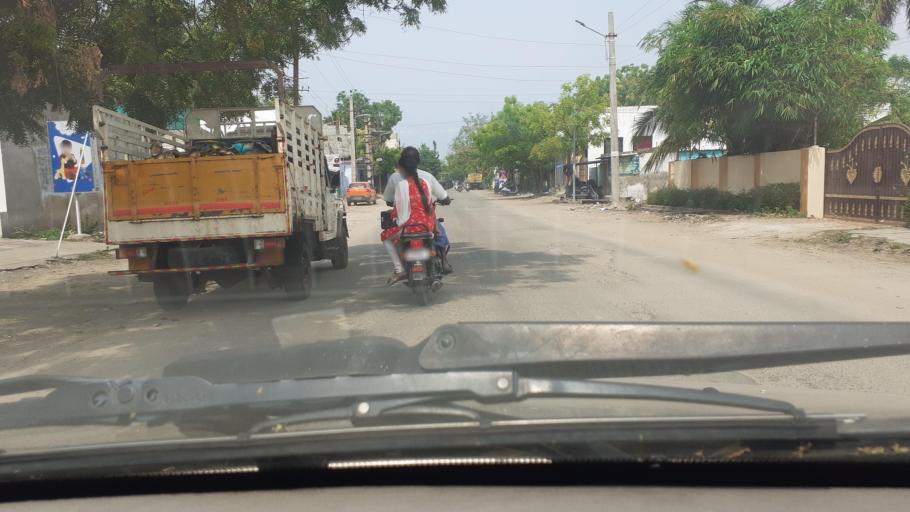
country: IN
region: Tamil Nadu
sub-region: Thoothukkudi
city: Korampallam
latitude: 8.8128
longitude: 78.1393
